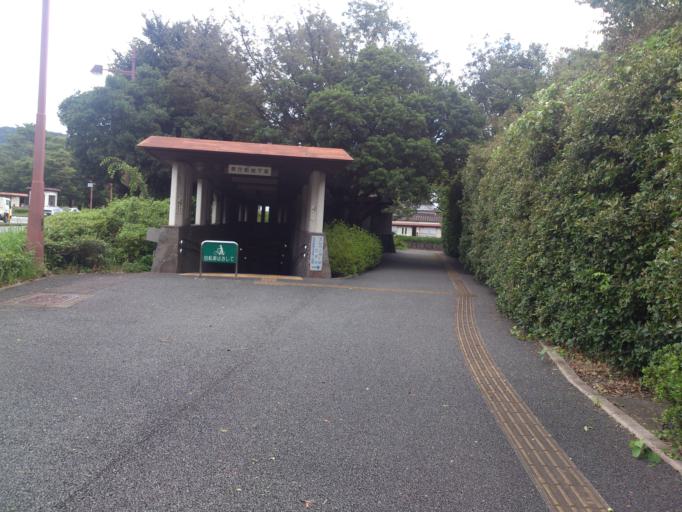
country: JP
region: Yamaguchi
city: Yamaguchi-shi
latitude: 34.1835
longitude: 131.4722
